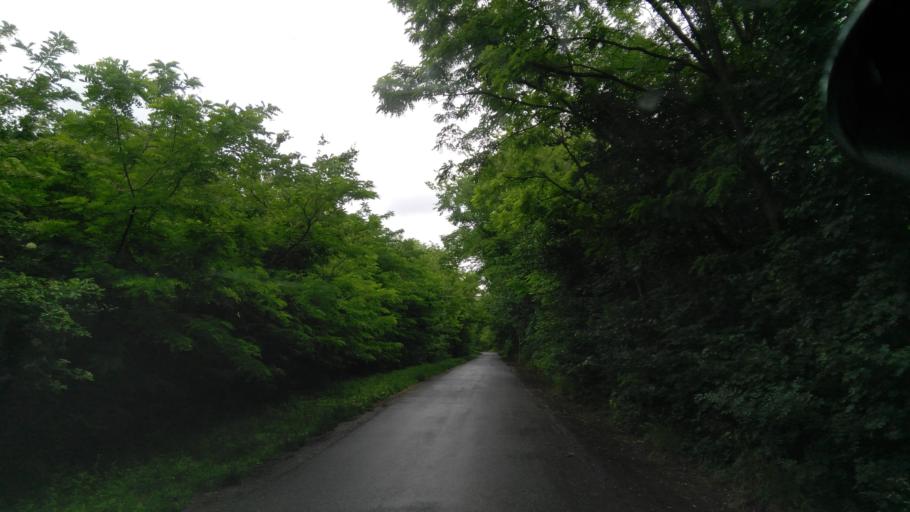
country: HU
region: Bekes
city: Doboz
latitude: 46.6785
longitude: 21.1855
